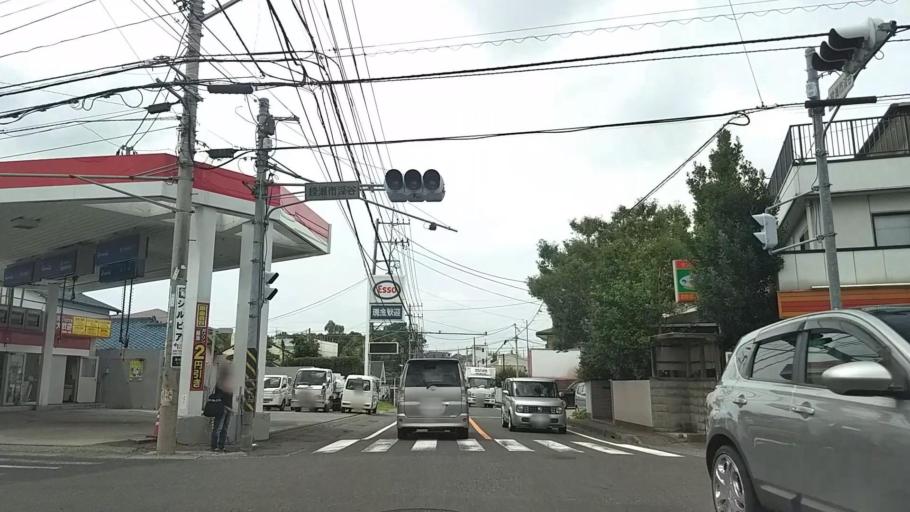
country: JP
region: Kanagawa
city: Minami-rinkan
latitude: 35.4305
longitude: 139.4364
